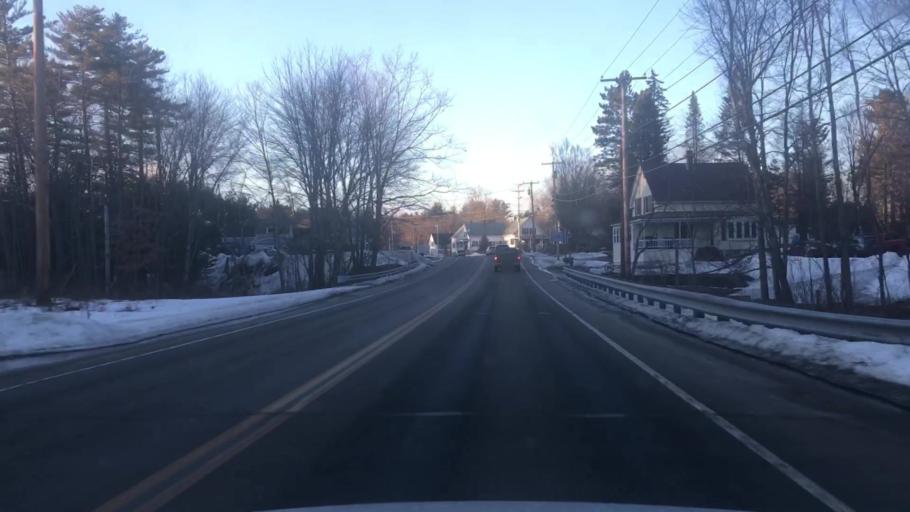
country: US
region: Maine
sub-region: York County
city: Springvale
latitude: 43.4746
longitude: -70.8109
